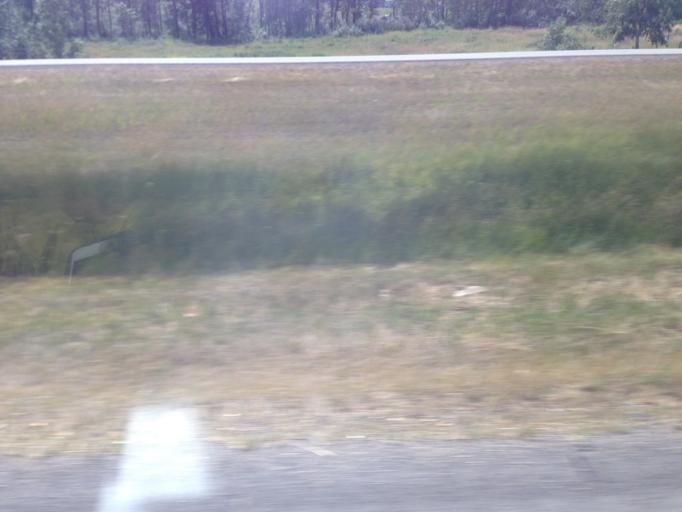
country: CA
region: Alberta
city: Cochrane
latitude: 51.0930
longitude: -114.5473
